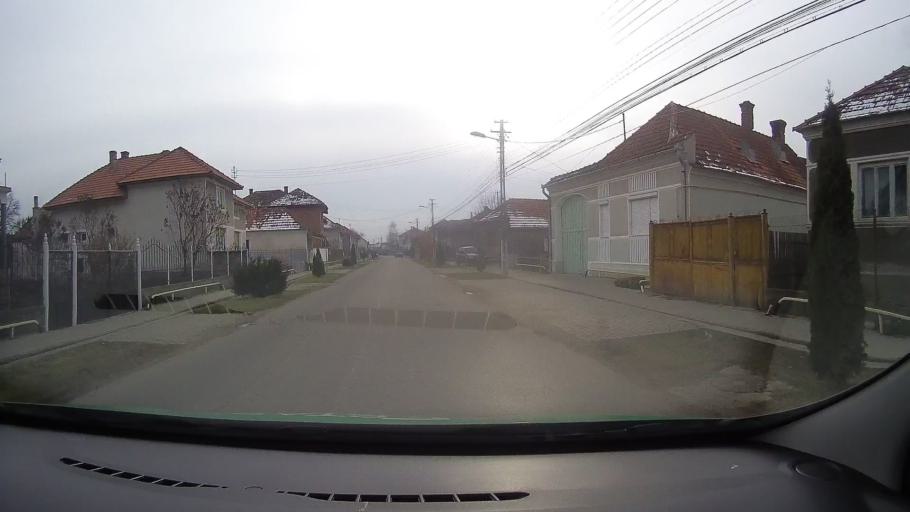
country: RO
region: Hunedoara
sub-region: Comuna Geoagiu
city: Geoagiu
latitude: 45.9296
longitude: 23.1962
